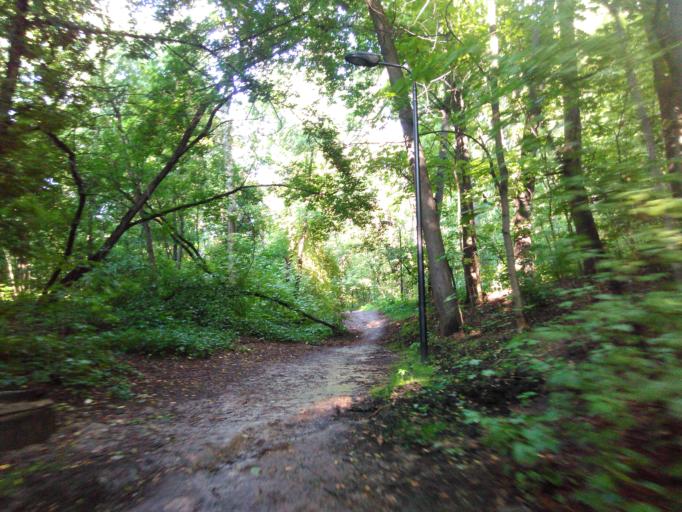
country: RU
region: Moskovskaya
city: Leninskiye Gory
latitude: 55.7092
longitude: 37.5666
